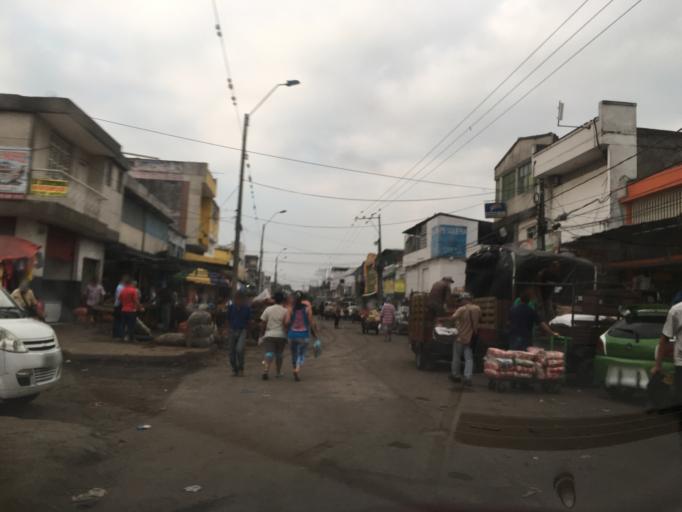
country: CO
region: Valle del Cauca
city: Cali
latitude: 3.4266
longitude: -76.5212
